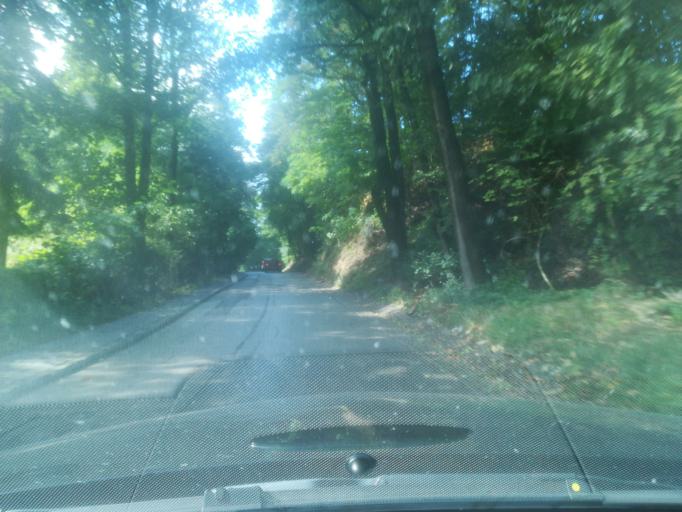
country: AT
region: Upper Austria
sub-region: Linz Stadt
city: Linz
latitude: 48.3350
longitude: 14.2807
